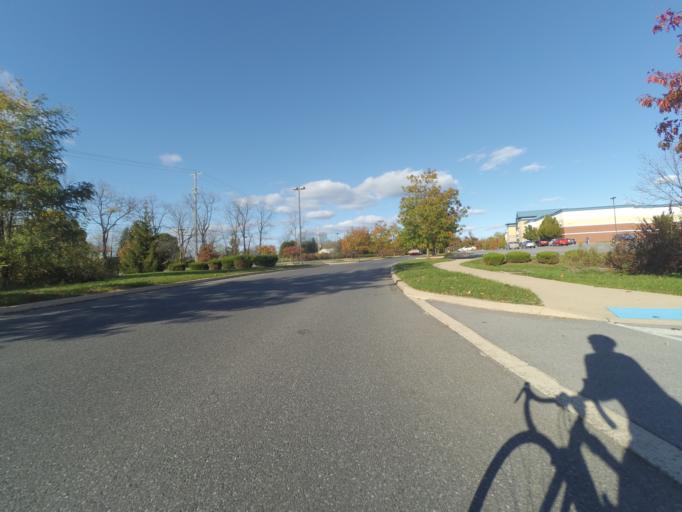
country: US
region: Pennsylvania
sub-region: Centre County
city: Houserville
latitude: 40.8395
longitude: -77.8023
